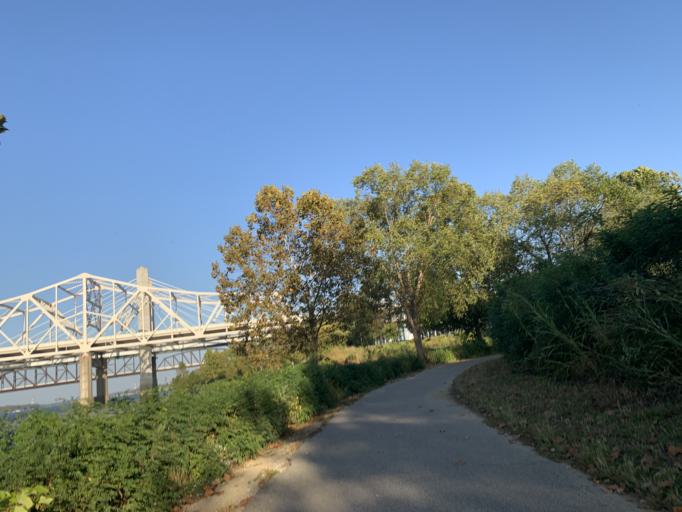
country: US
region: Kentucky
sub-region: Jefferson County
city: Louisville
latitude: 38.2609
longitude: -85.7448
